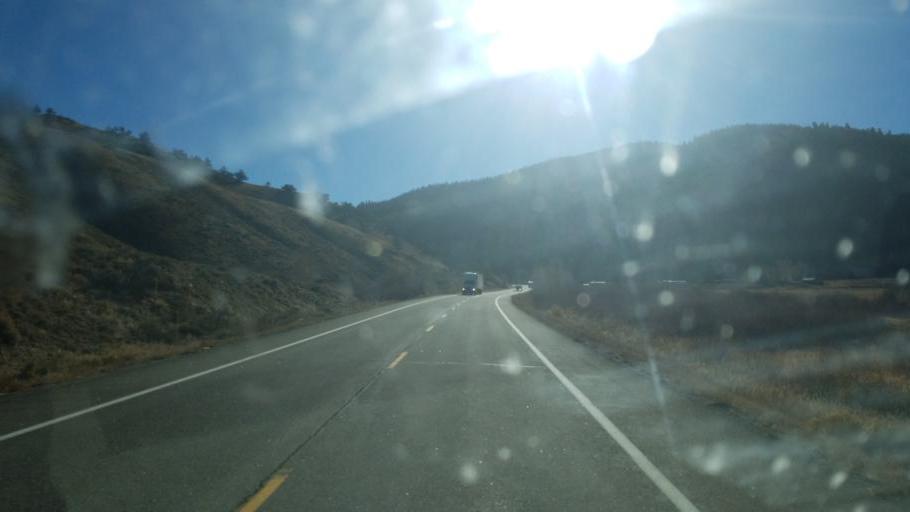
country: US
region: Colorado
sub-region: Saguache County
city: Saguache
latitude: 38.3920
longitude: -106.4572
